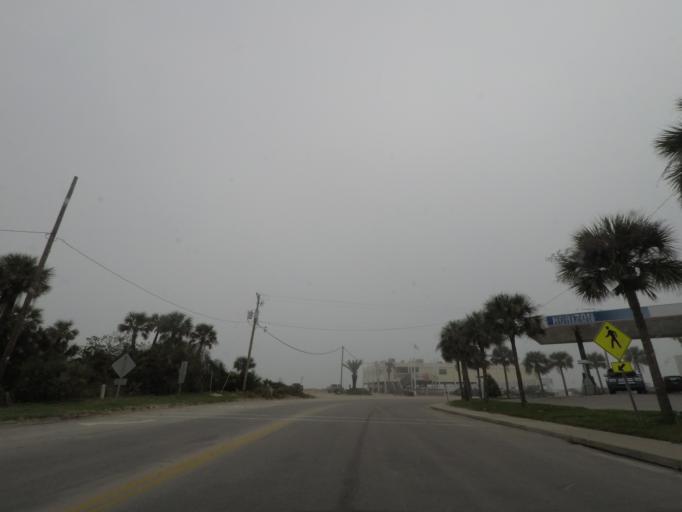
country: US
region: South Carolina
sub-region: Charleston County
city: Seabrook Island
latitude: 32.5038
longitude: -80.2968
